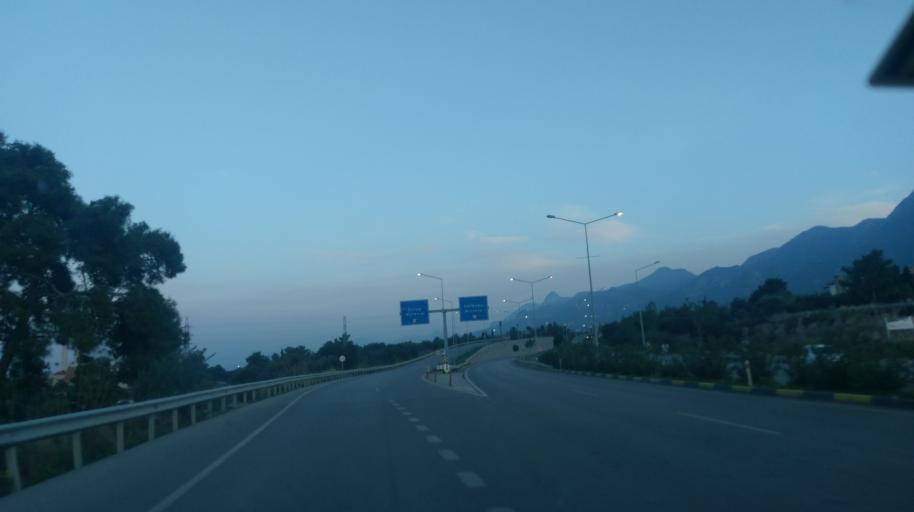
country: CY
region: Keryneia
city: Kyrenia
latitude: 35.3273
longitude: 33.3140
